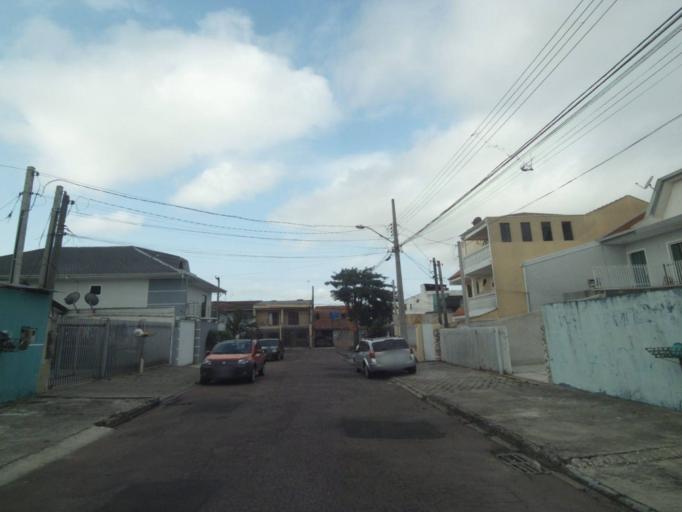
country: BR
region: Parana
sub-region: Sao Jose Dos Pinhais
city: Sao Jose dos Pinhais
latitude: -25.5470
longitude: -49.2585
